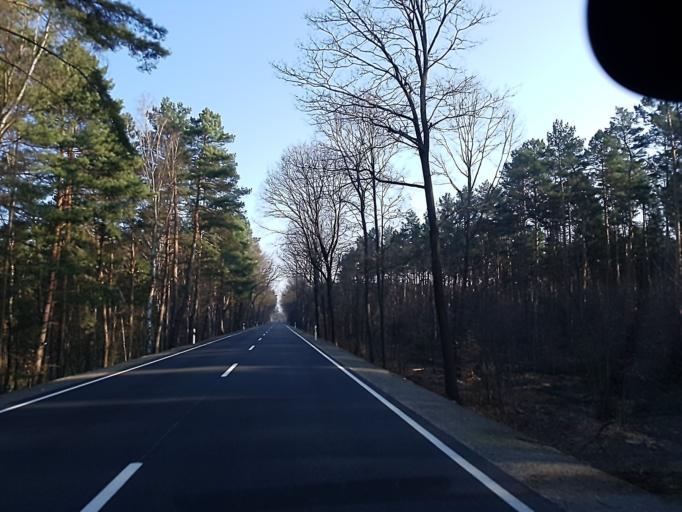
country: DE
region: Brandenburg
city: Bronkow
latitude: 51.6929
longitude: 13.9178
